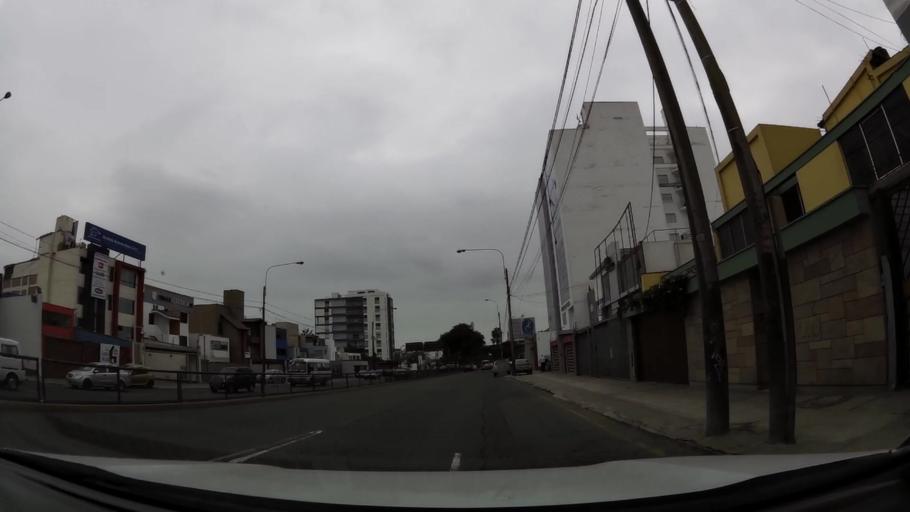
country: PE
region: Lima
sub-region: Lima
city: Surco
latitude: -12.1284
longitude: -77.0040
